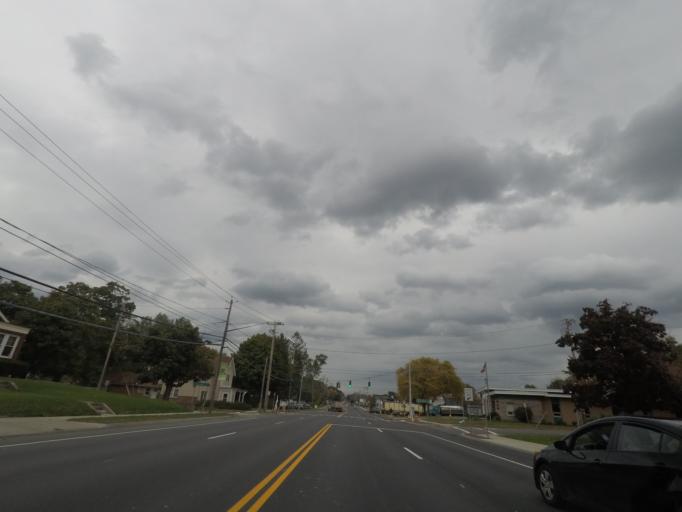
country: US
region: New York
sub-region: Albany County
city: McKownville
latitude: 42.6791
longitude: -73.8313
